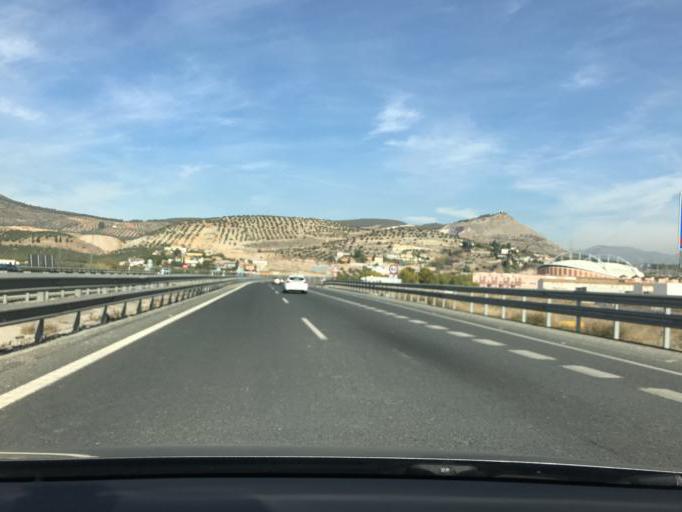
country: ES
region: Andalusia
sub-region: Provincia de Granada
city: Atarfe
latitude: 37.2214
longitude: -3.7066
